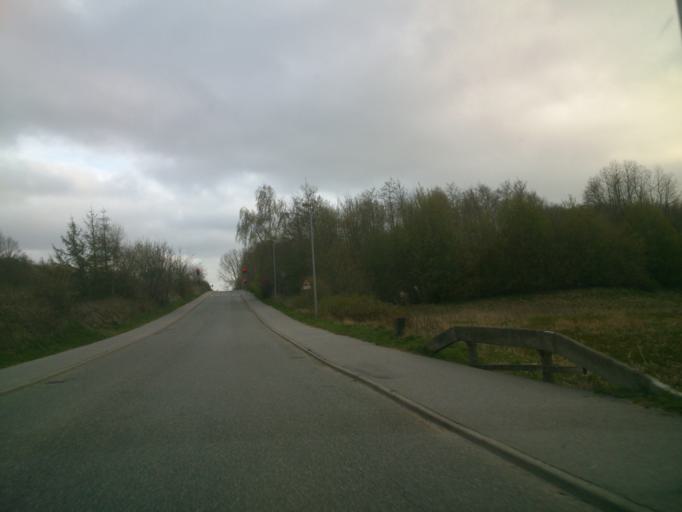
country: DK
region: South Denmark
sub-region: Fredericia Kommune
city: Fredericia
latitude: 55.5732
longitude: 9.7093
